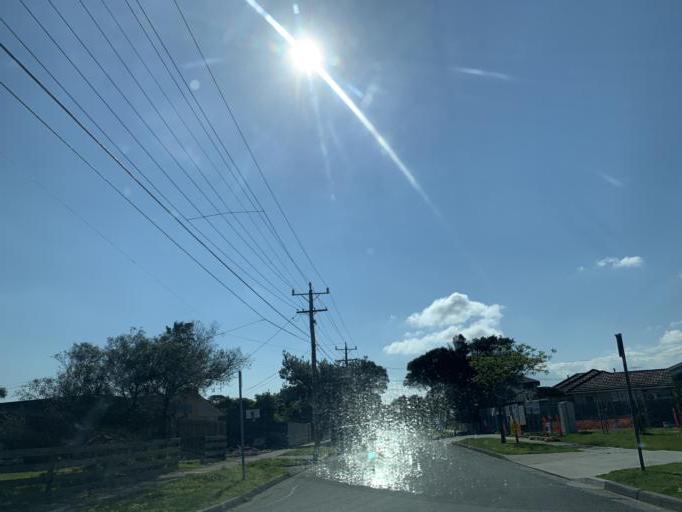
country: AU
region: Victoria
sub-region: Kingston
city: Aspendale
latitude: -38.0141
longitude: 145.0964
